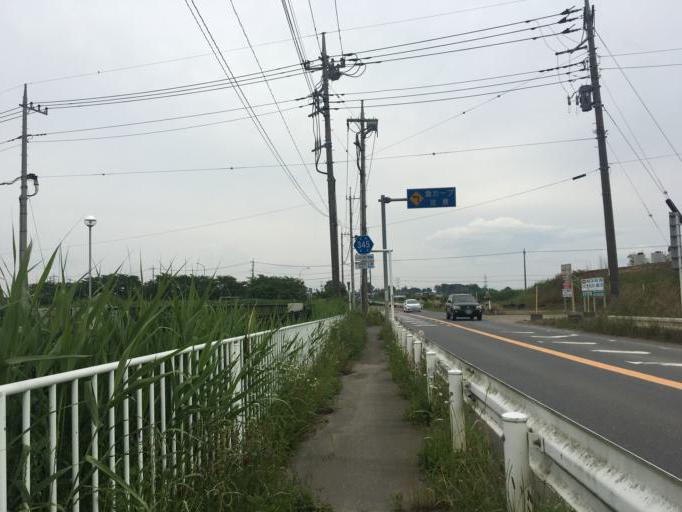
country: JP
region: Saitama
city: Sakado
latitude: 36.0193
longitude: 139.4394
